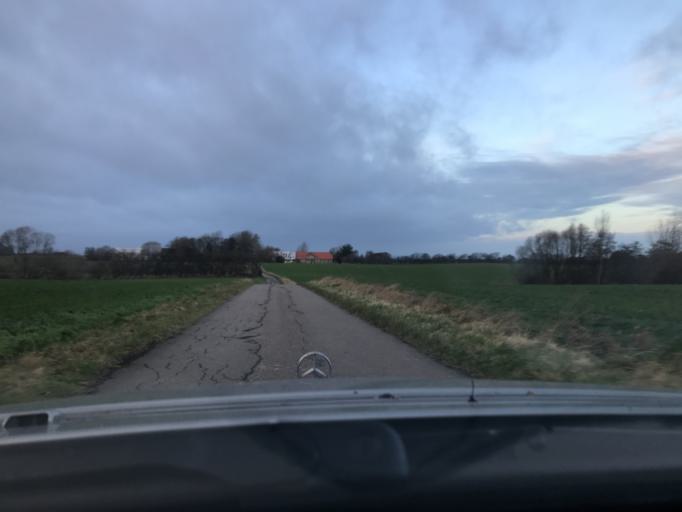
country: DK
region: South Denmark
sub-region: Sonderborg Kommune
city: Nordborg
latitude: 55.0651
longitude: 9.6940
